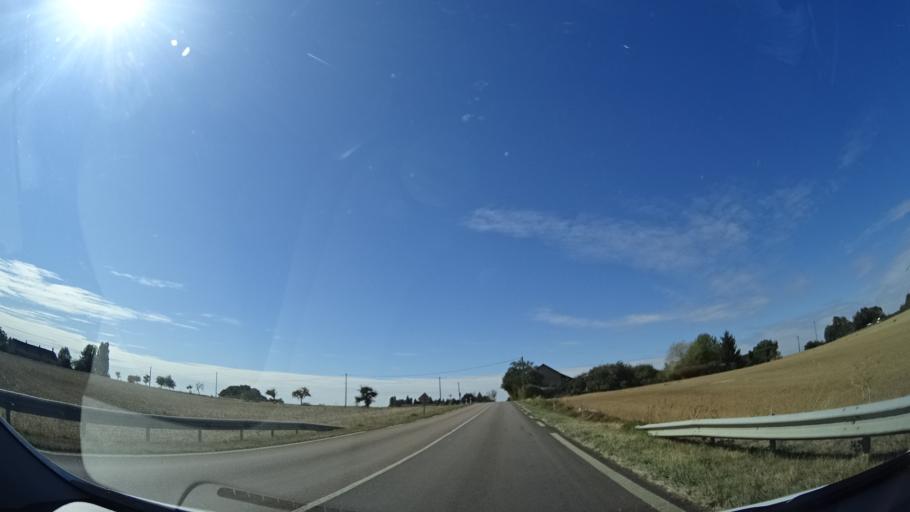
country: FR
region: Bourgogne
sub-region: Departement de l'Yonne
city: Charny
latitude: 47.9338
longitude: 3.1624
